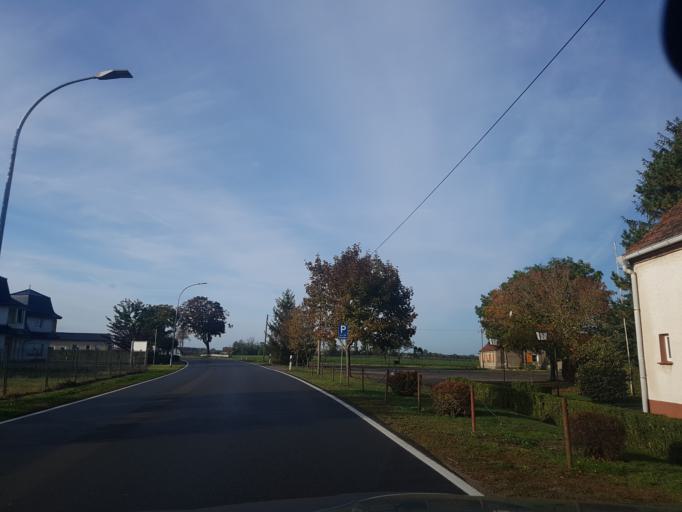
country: DE
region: Saxony
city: Arzberg
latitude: 51.6142
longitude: 13.1441
